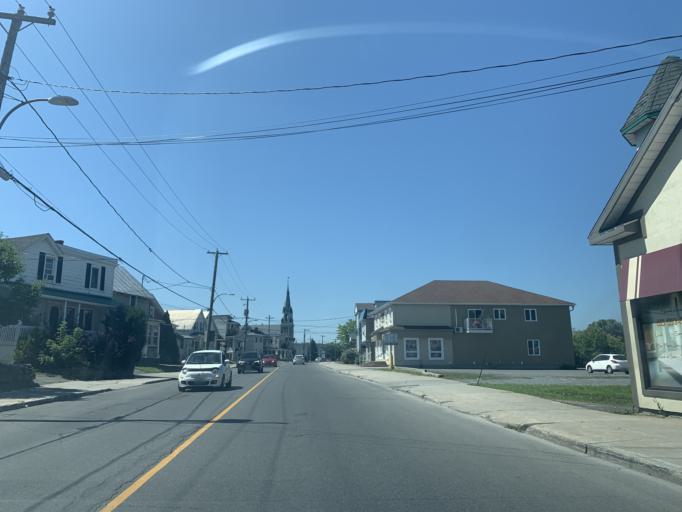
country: CA
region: Ontario
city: Hawkesbury
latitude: 45.6104
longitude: -74.6002
